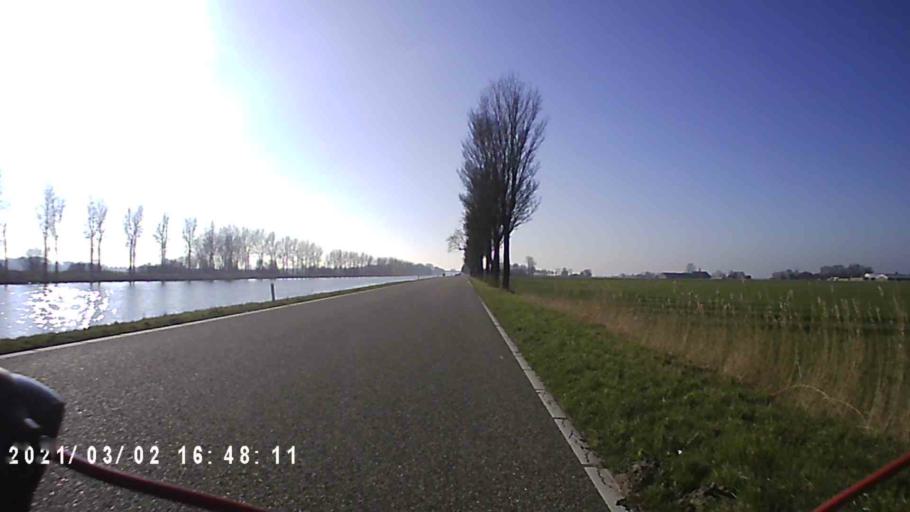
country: NL
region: Groningen
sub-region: Gemeente Grootegast
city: Grootegast
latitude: 53.2449
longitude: 6.2709
